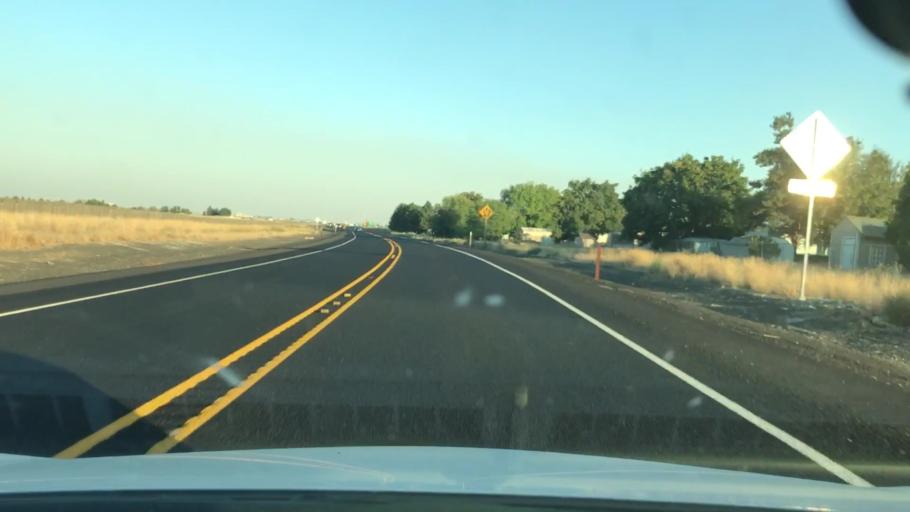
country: US
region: Washington
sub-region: Grant County
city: Cascade Valley
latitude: 47.1604
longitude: -119.3214
